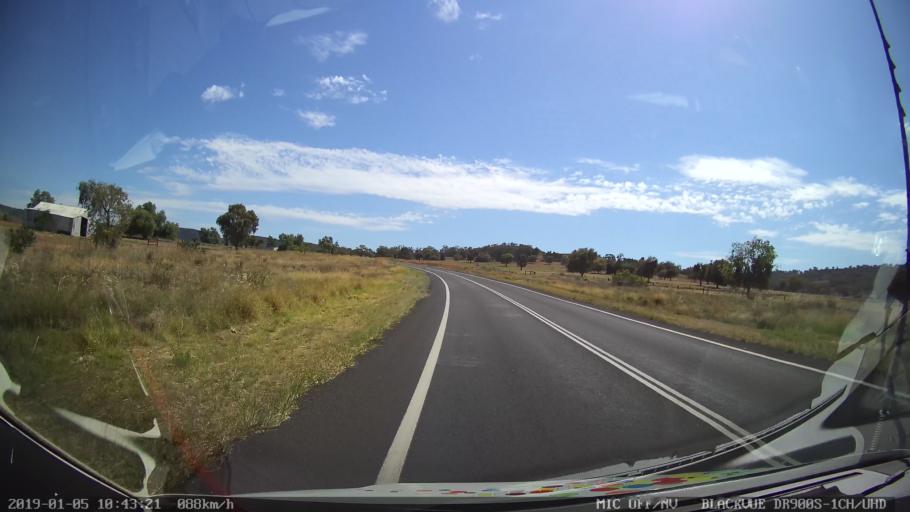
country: AU
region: New South Wales
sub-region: Warrumbungle Shire
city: Coonabarabran
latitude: -31.4656
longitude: 148.9873
